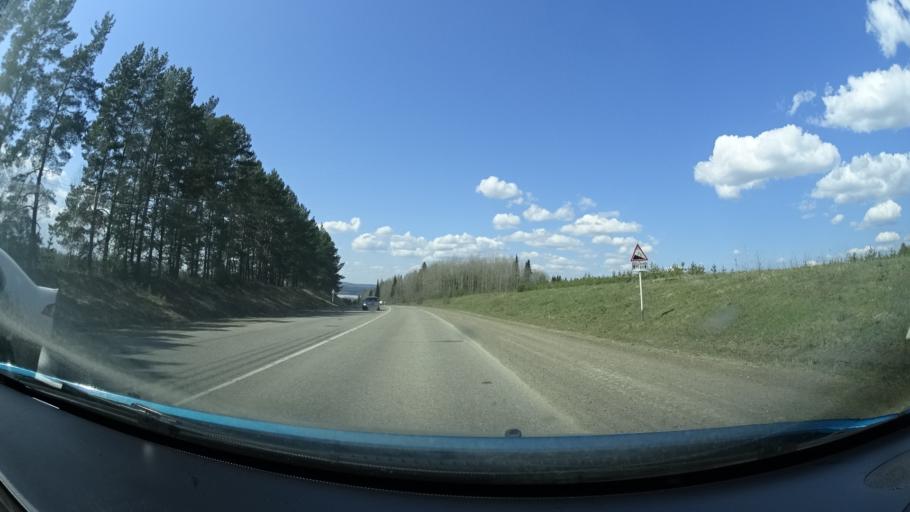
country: RU
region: Perm
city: Osa
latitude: 57.3239
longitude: 55.6130
